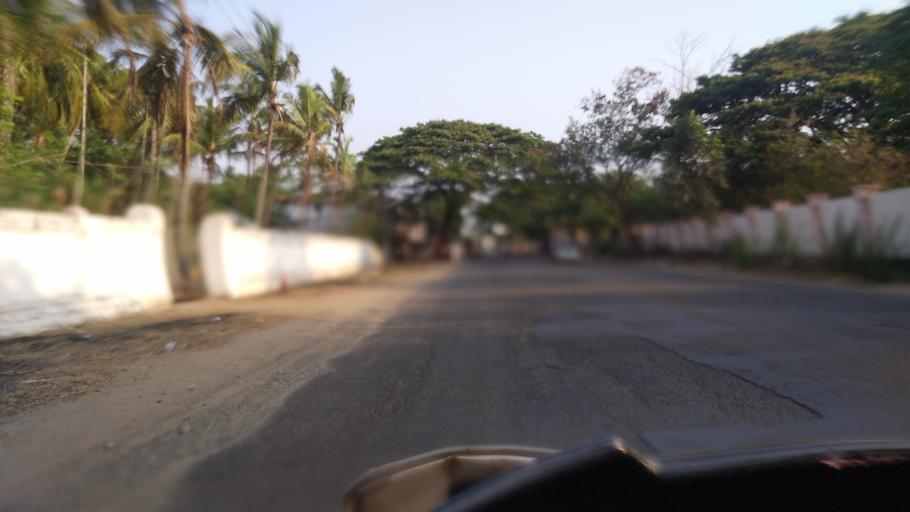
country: IN
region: Kerala
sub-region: Thrissur District
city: Thanniyam
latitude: 10.4248
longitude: 76.1027
